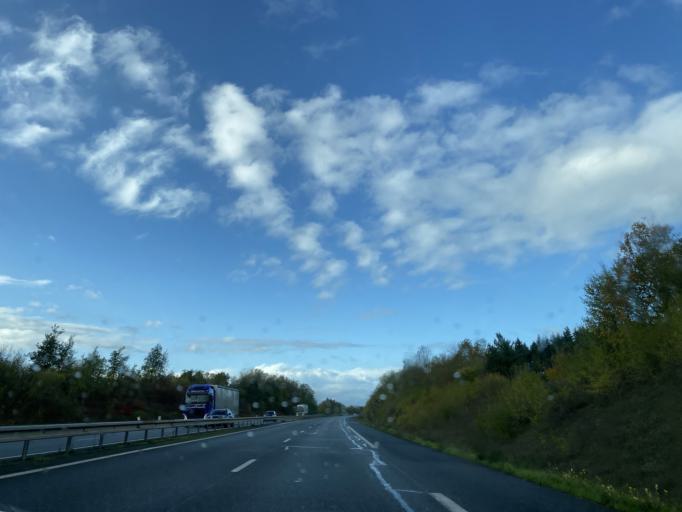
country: FR
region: Centre
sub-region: Departement du Cher
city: Mehun-sur-Yevre
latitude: 47.1131
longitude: 2.2009
